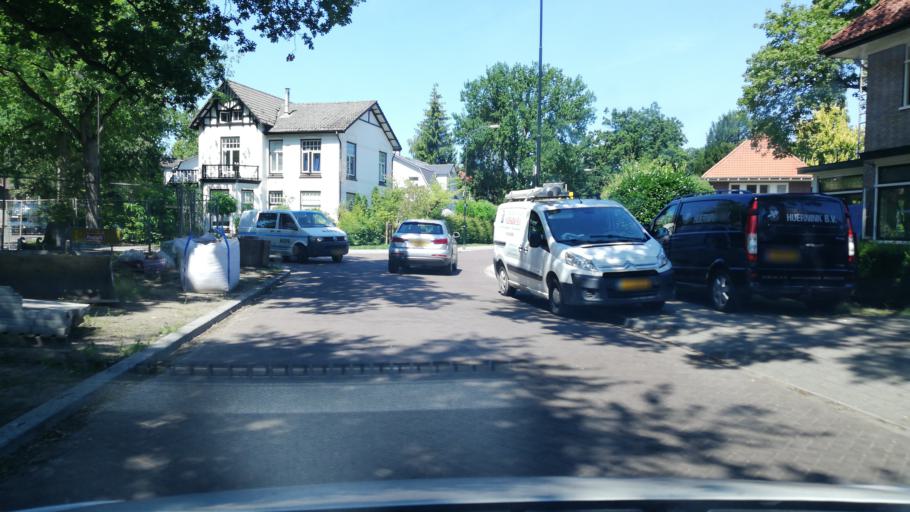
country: NL
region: Gelderland
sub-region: Gemeente Apeldoorn
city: Apeldoorn
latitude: 52.2244
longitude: 5.9616
